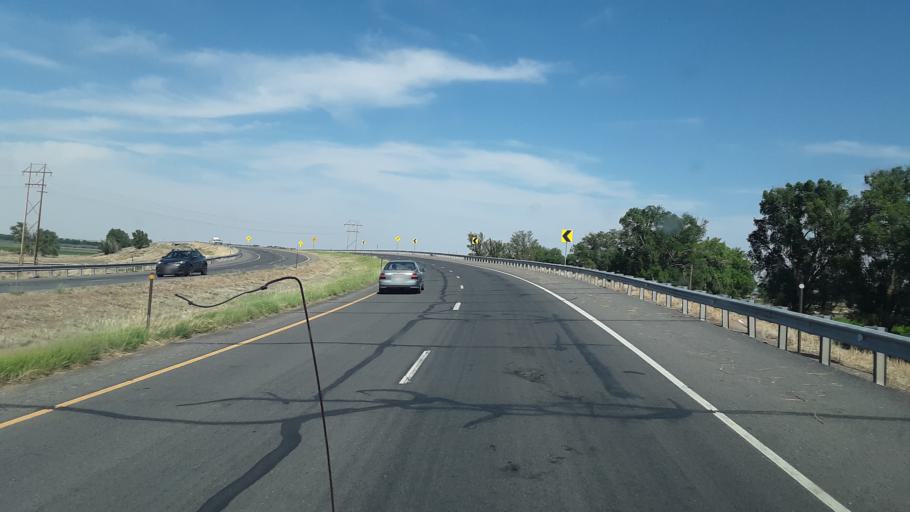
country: US
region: Colorado
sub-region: Otero County
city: Rocky Ford
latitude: 38.1022
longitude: -103.8470
